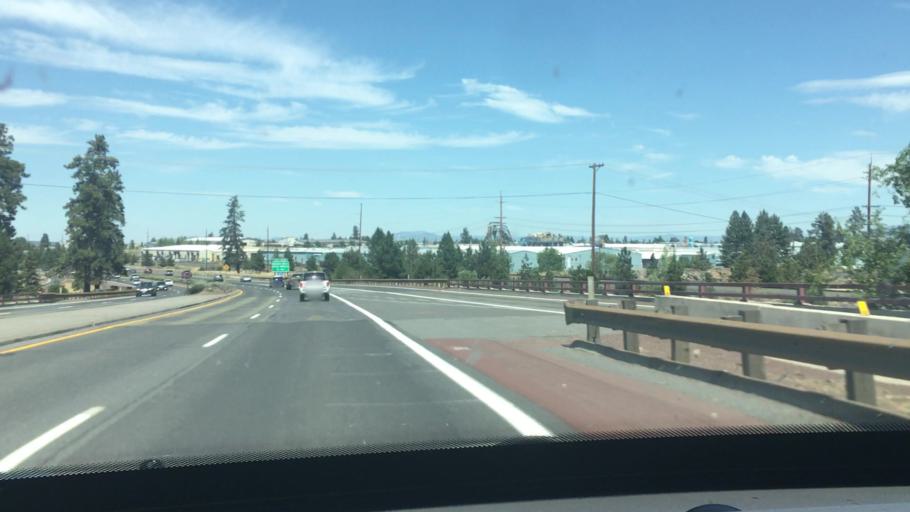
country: US
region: Oregon
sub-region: Deschutes County
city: Bend
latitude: 44.0783
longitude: -121.3024
